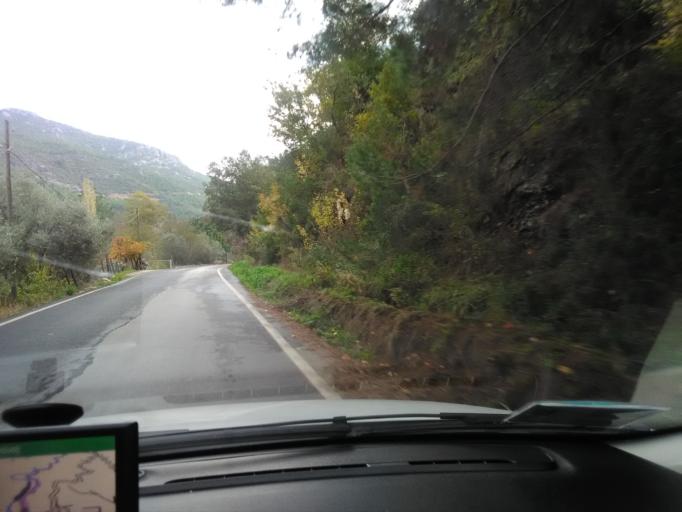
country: TR
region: Antalya
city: Gazipasa
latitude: 36.2615
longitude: 32.3805
